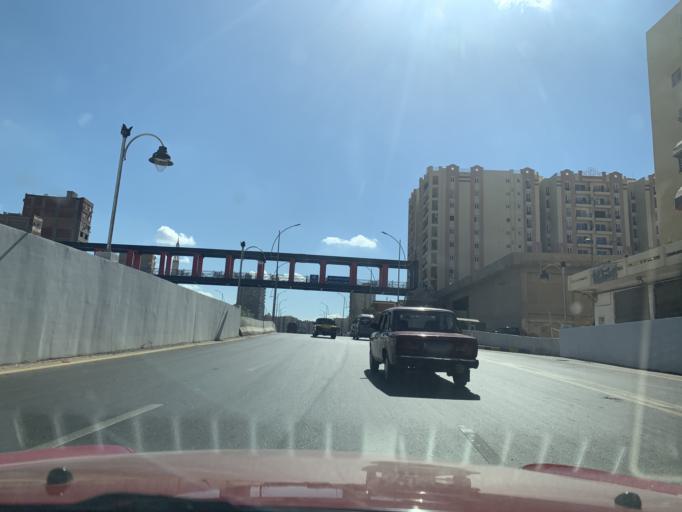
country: EG
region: Alexandria
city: Alexandria
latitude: 31.2173
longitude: 29.9633
